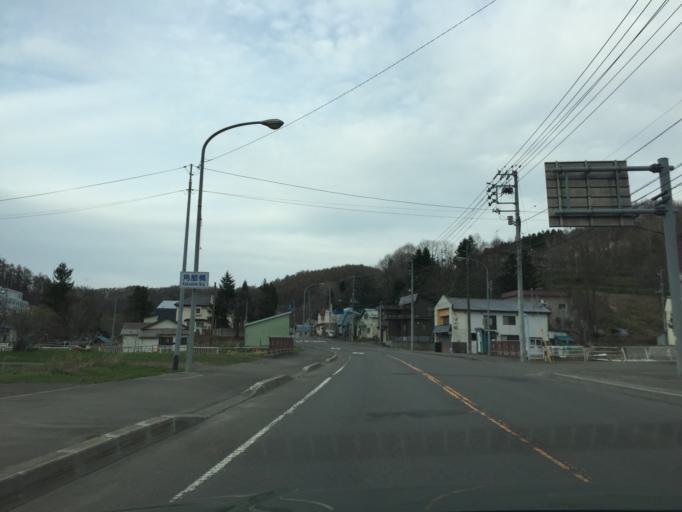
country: JP
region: Hokkaido
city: Utashinai
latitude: 43.5078
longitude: 142.0227
